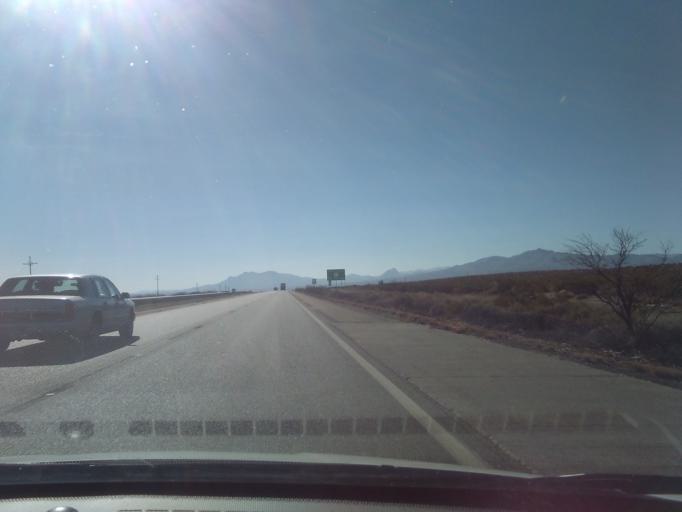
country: US
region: New Mexico
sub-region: Socorro County
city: Socorro
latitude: 34.2823
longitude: -106.8984
